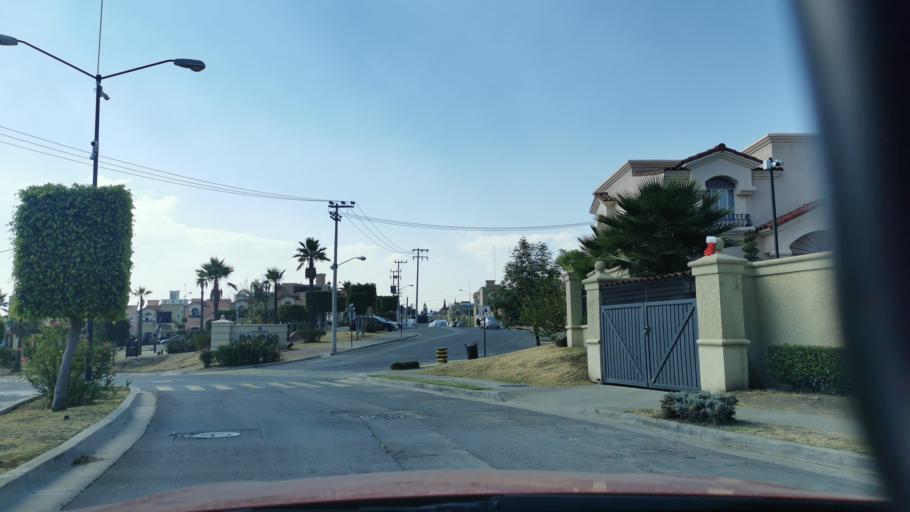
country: MX
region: Mexico
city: Cuautitlan Izcalli
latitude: 19.6440
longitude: -99.2174
